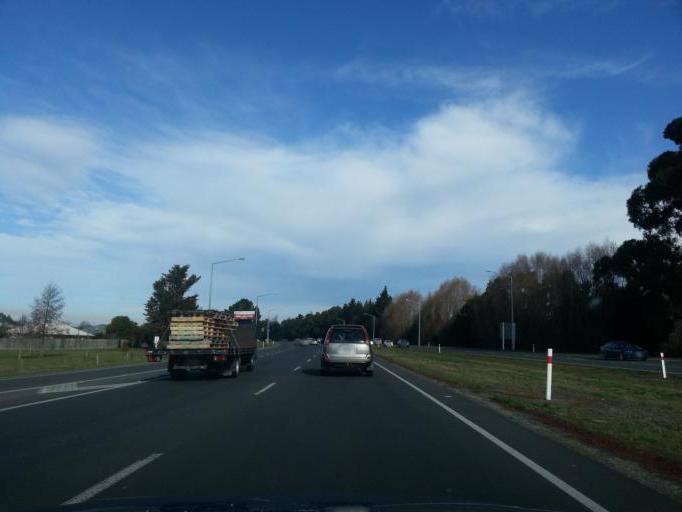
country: NZ
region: Canterbury
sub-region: Waimakariri District
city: Kaiapoi
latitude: -43.3890
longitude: 172.6401
